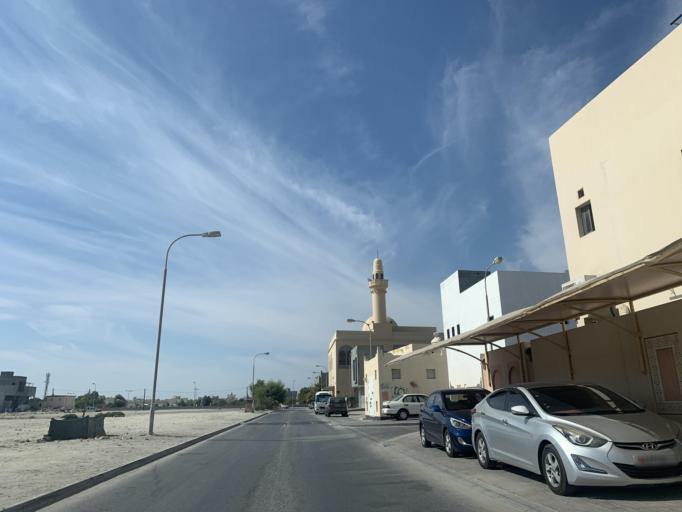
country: BH
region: Central Governorate
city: Madinat Hamad
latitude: 26.1161
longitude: 50.4873
